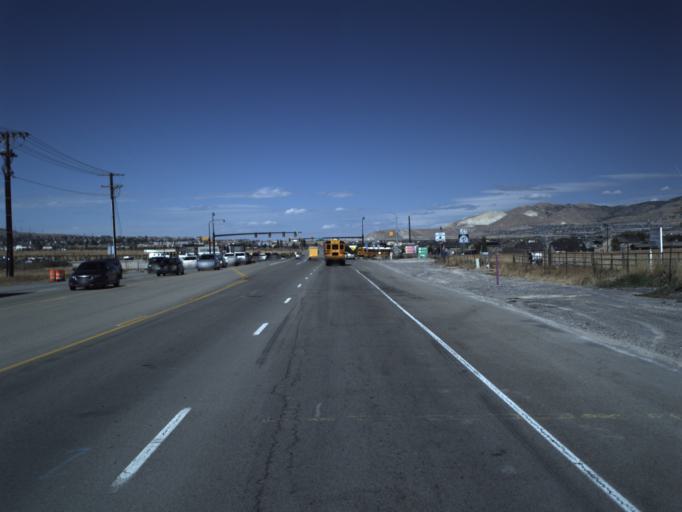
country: US
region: Utah
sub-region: Utah County
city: Saratoga Springs
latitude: 40.3702
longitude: -111.9163
